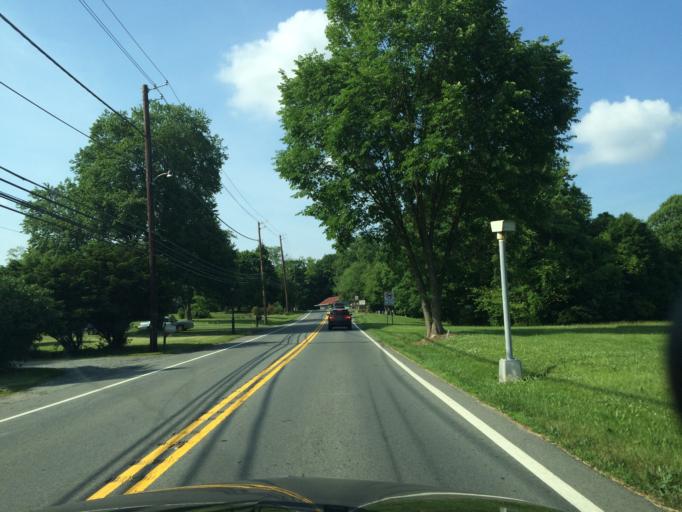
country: US
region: Maryland
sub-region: Montgomery County
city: Olney
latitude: 39.1771
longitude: -77.0582
